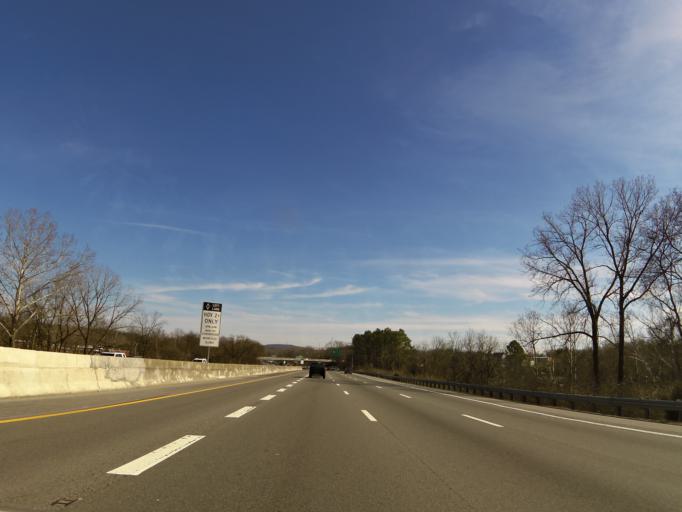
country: US
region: Tennessee
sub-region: Rutherford County
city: La Vergne
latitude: 36.0562
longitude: -86.6760
